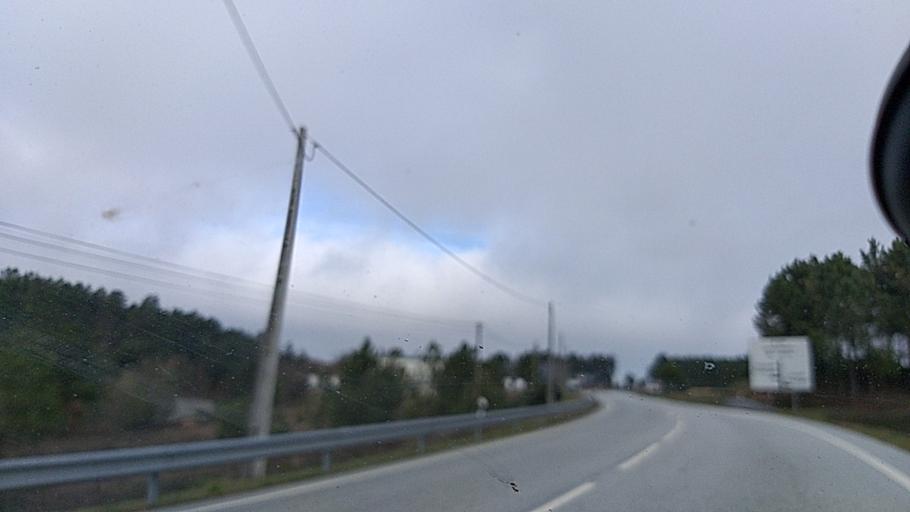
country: PT
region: Guarda
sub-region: Aguiar da Beira
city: Aguiar da Beira
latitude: 40.7870
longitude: -7.5024
